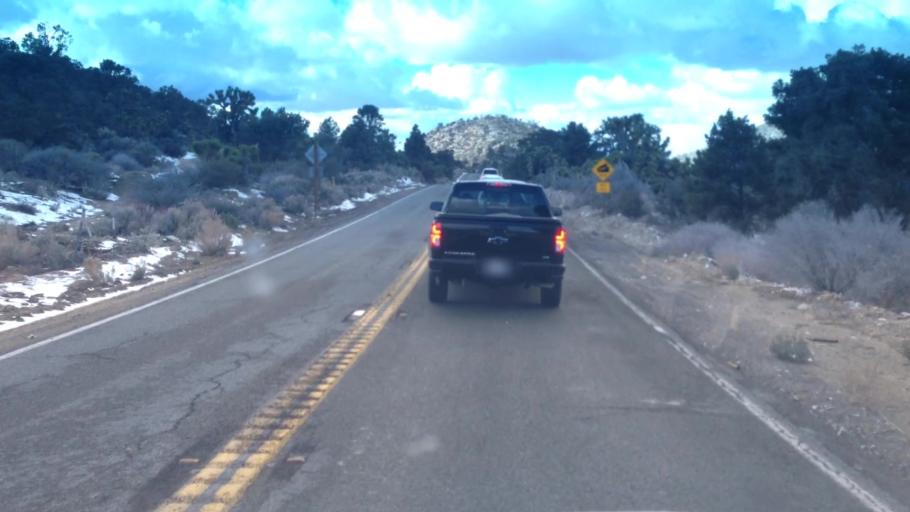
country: US
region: California
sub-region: San Bernardino County
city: Big Bear City
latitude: 34.3223
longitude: -116.8186
